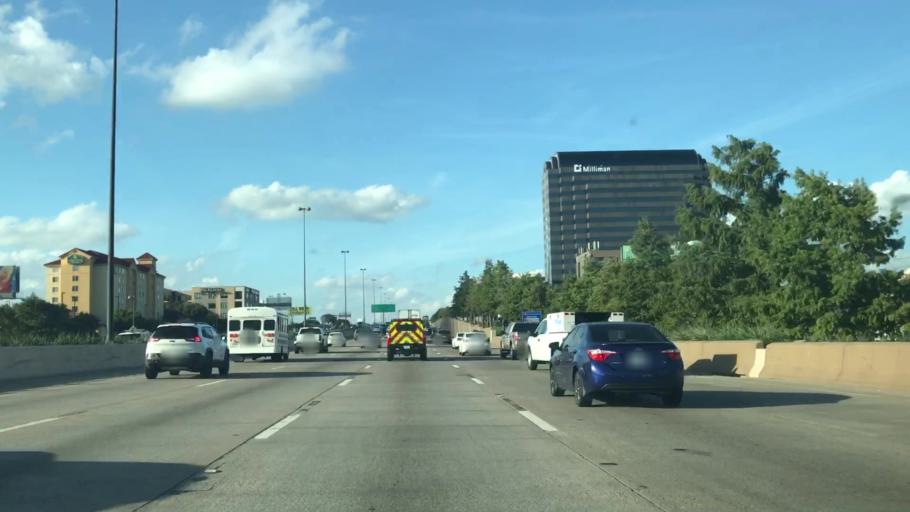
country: US
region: Texas
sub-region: Dallas County
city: University Park
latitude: 32.8807
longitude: -96.7700
